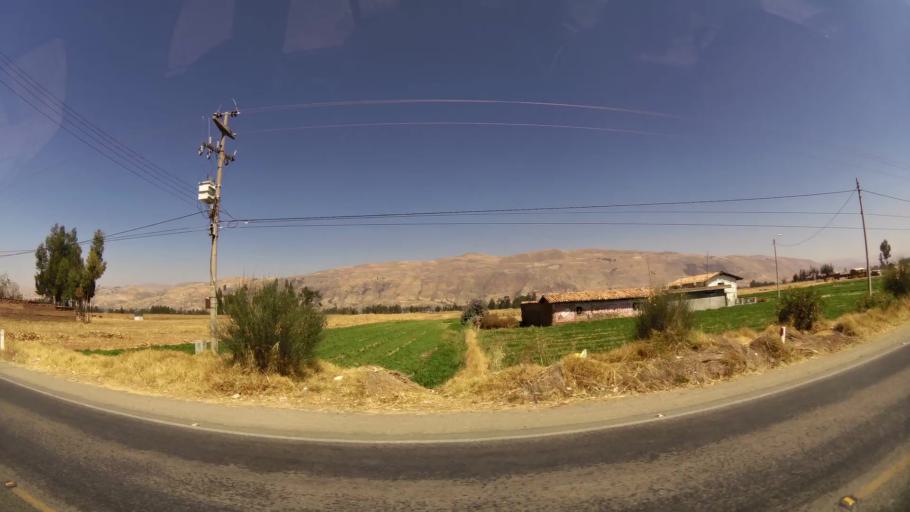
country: PE
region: Junin
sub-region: Provincia de Jauja
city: San Lorenzo
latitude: -11.8371
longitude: -75.3932
